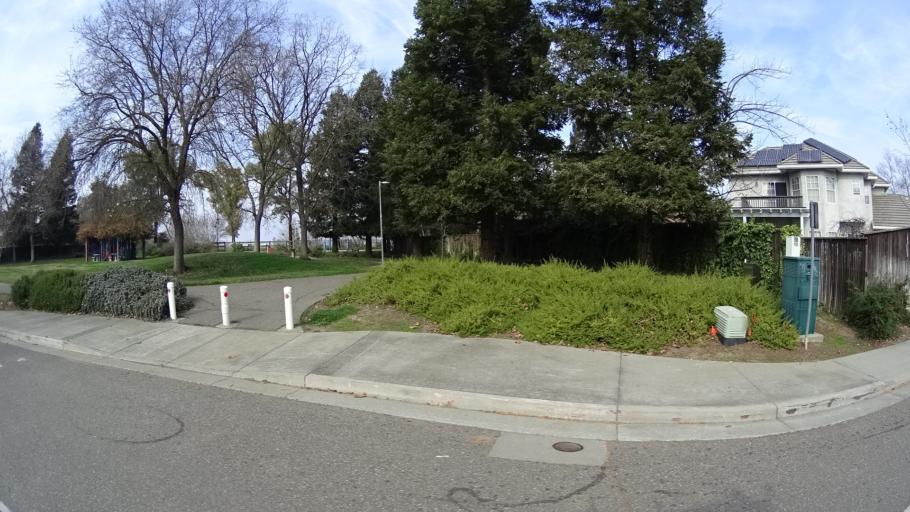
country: US
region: California
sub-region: Yolo County
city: Davis
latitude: 38.5713
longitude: -121.7574
